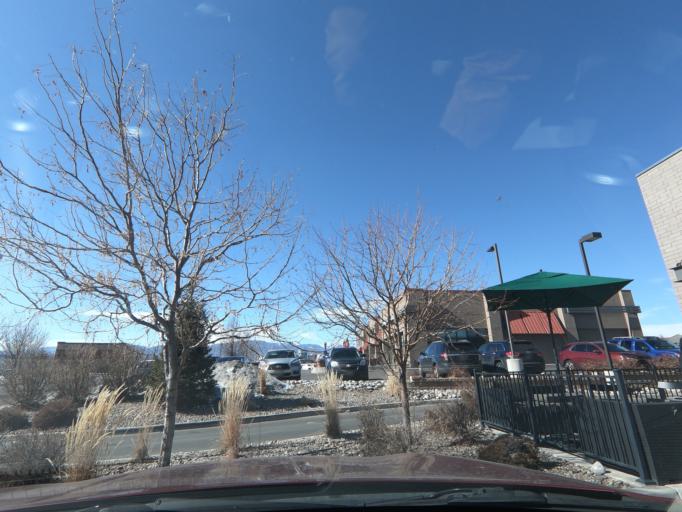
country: US
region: Colorado
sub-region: El Paso County
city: Security-Widefield
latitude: 38.7181
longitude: -104.6996
